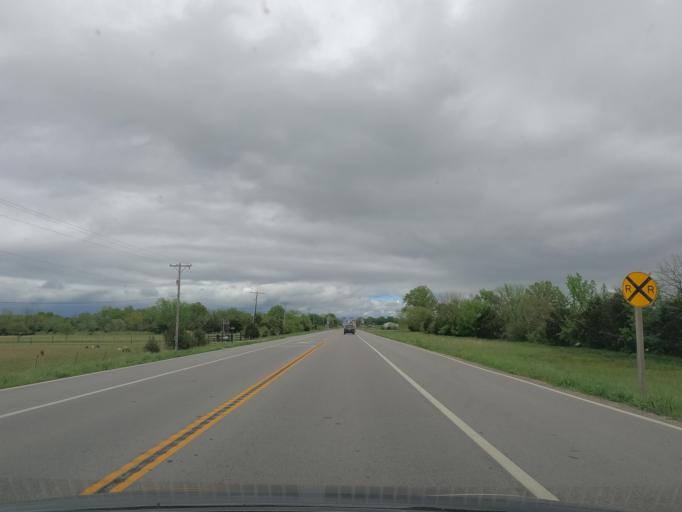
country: US
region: Kansas
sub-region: Crawford County
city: Pittsburg
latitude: 37.3393
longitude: -94.8198
